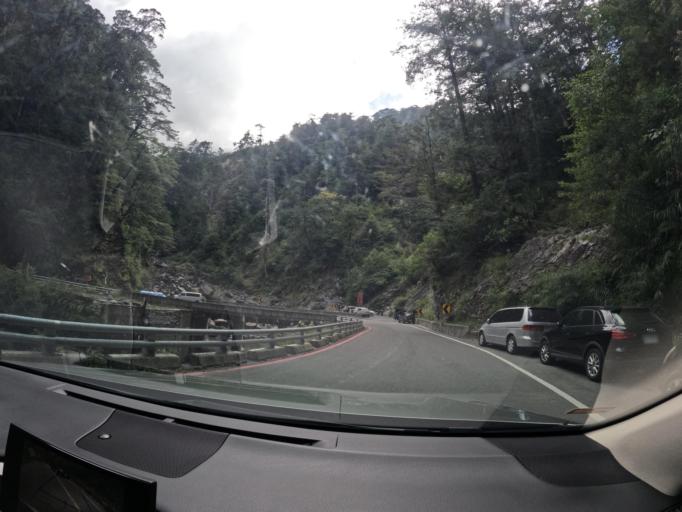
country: TW
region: Taiwan
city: Yujing
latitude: 23.2581
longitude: 120.9185
